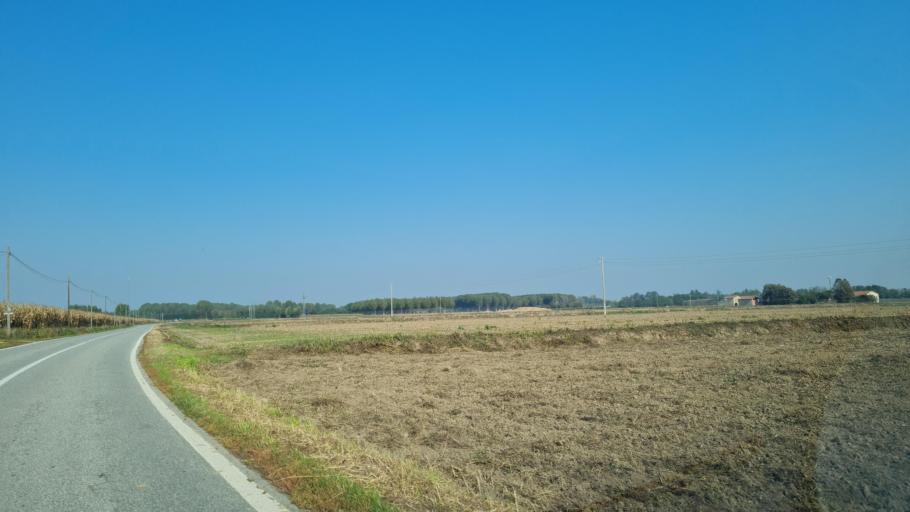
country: IT
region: Piedmont
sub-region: Provincia di Novara
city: Landiona
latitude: 45.4893
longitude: 8.4331
